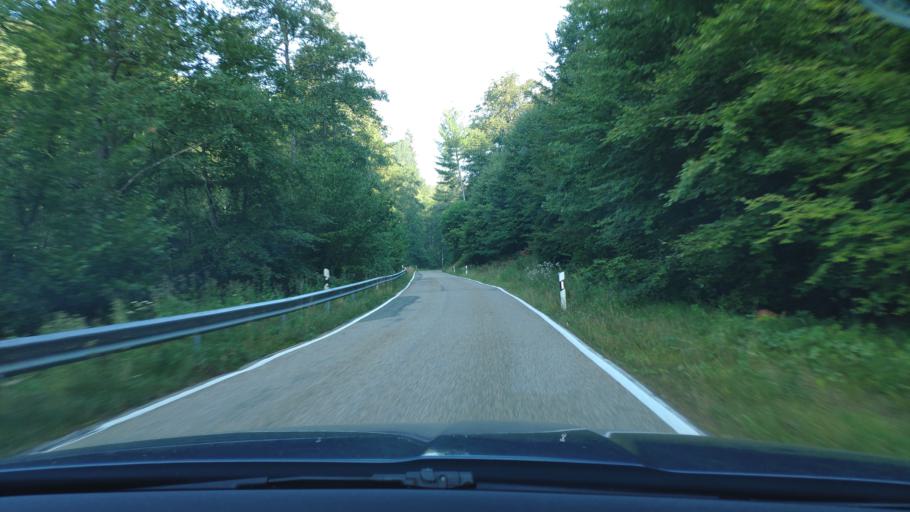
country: DE
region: Rheinland-Pfalz
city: Ludwigswinkel
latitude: 49.0969
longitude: 7.6306
